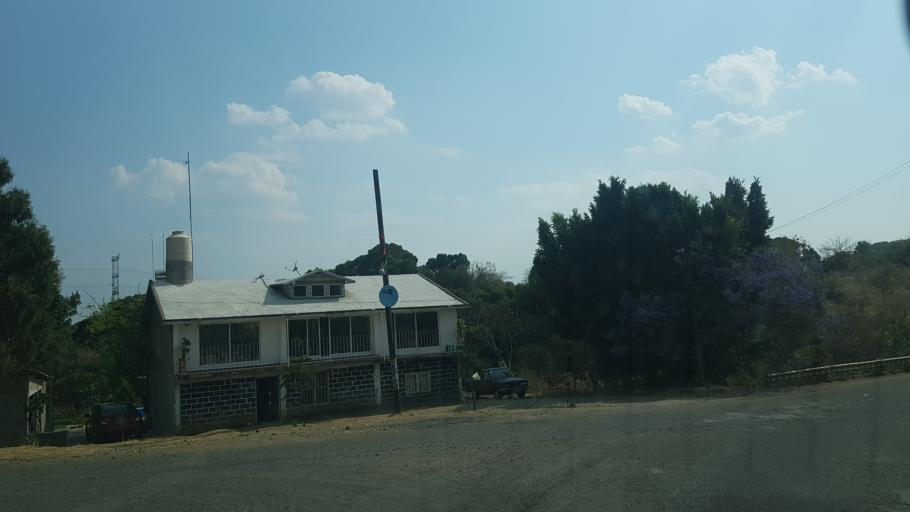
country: MX
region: Puebla
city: San Juan Amecac
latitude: 18.8302
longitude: -98.7052
